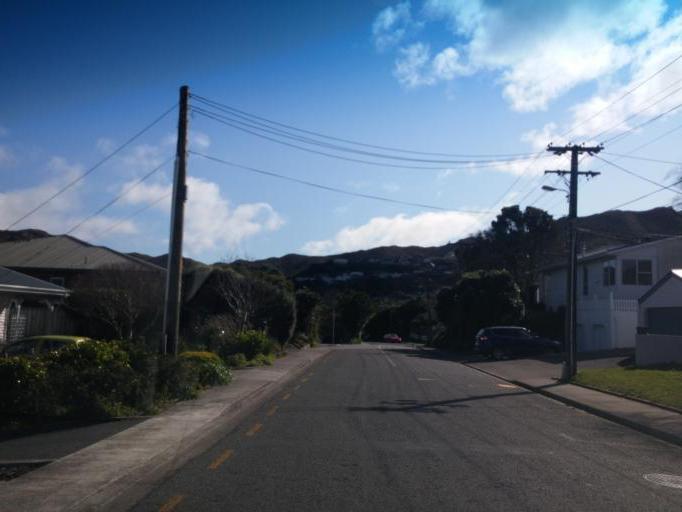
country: NZ
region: Wellington
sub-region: Wellington City
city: Wellington
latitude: -41.2483
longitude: 174.7848
